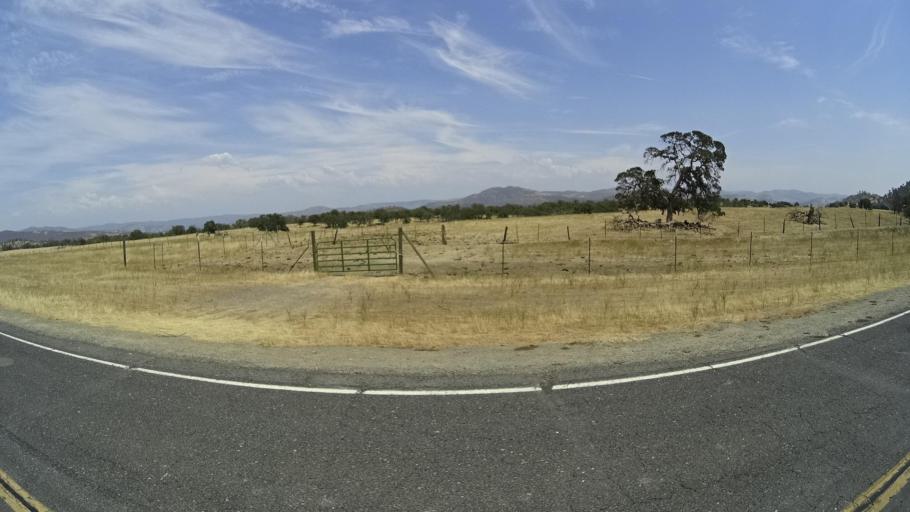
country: US
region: California
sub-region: Tuolumne County
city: Tuolumne City
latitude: 37.6388
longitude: -120.3067
